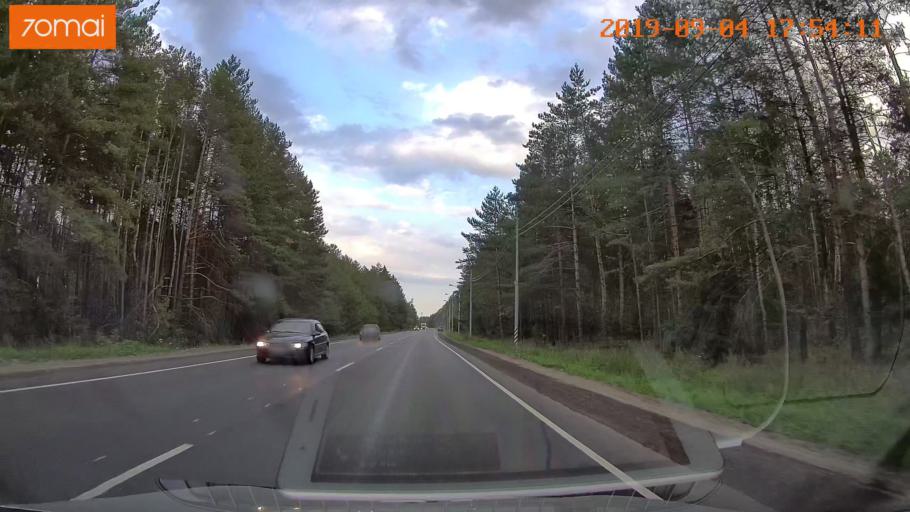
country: RU
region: Moskovskaya
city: Imeni Tsyurupy
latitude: 55.5120
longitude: 38.7383
